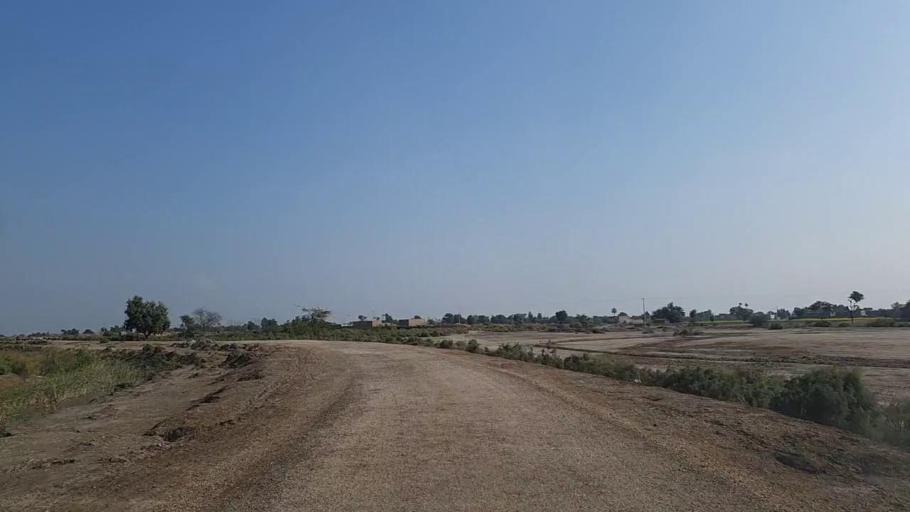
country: PK
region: Sindh
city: Jam Sahib
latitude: 26.2873
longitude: 68.6014
